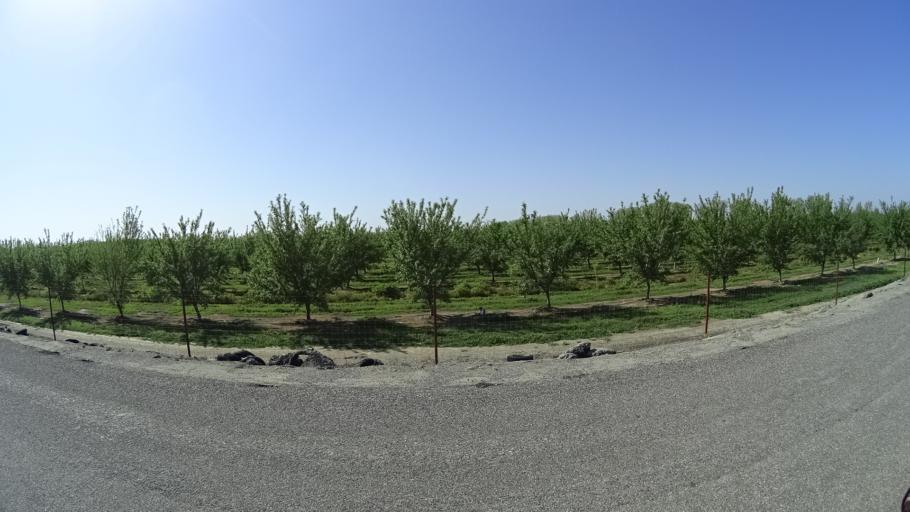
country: US
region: California
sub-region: Glenn County
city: Hamilton City
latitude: 39.6595
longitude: -121.9950
